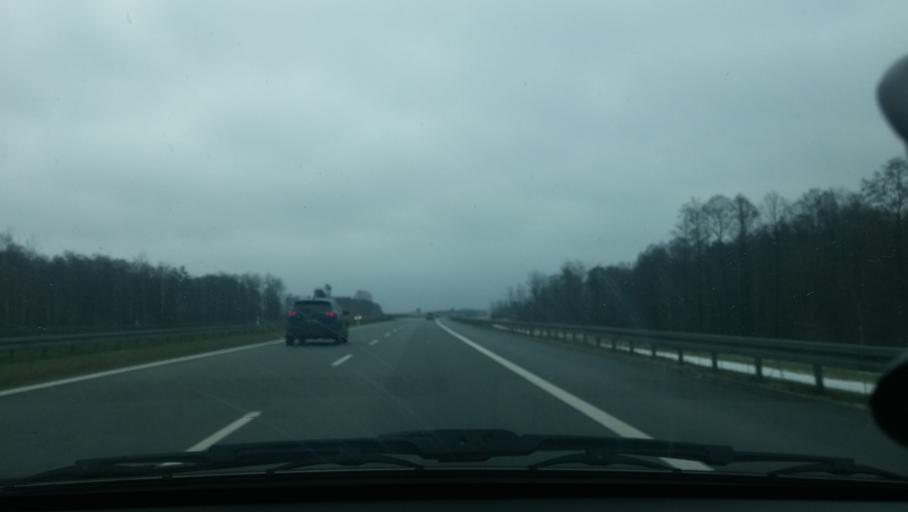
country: PL
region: Masovian Voivodeship
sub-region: Powiat minski
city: Ceglow
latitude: 52.2031
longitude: 21.7402
